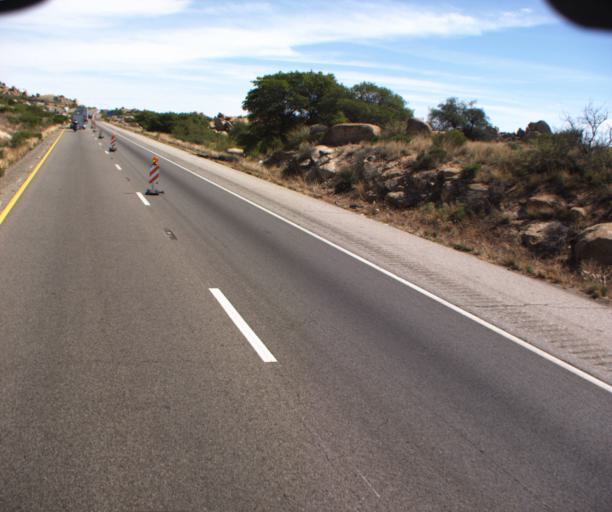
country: US
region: Arizona
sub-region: Cochise County
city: Saint David
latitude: 32.0532
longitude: -110.0836
